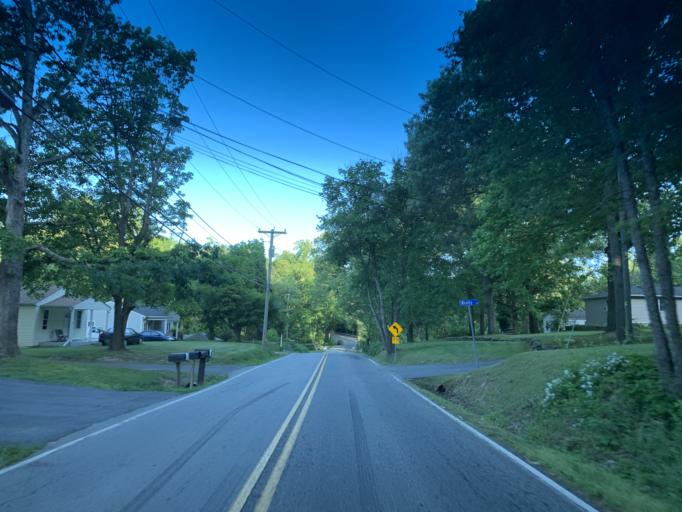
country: US
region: Maryland
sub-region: Cecil County
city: Elkton
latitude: 39.6644
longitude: -75.8375
